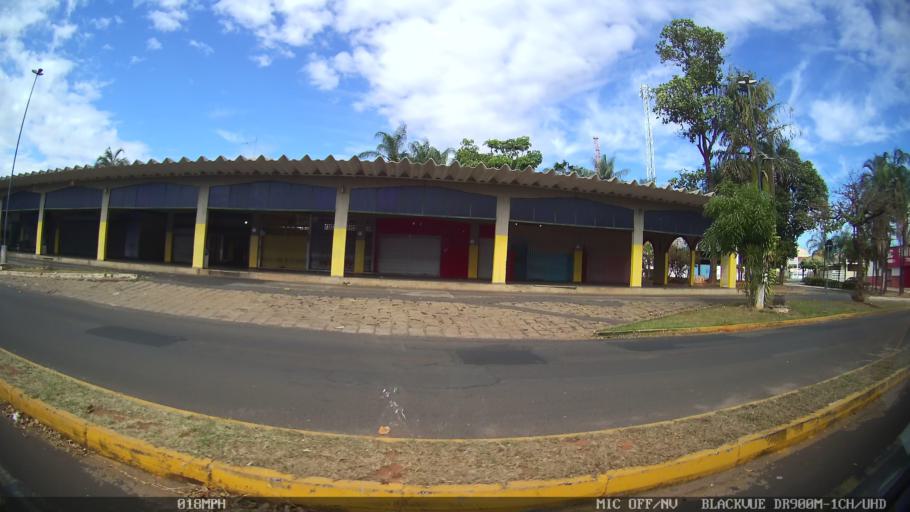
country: BR
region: Sao Paulo
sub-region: Bady Bassitt
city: Bady Bassitt
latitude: -20.8140
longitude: -49.5147
